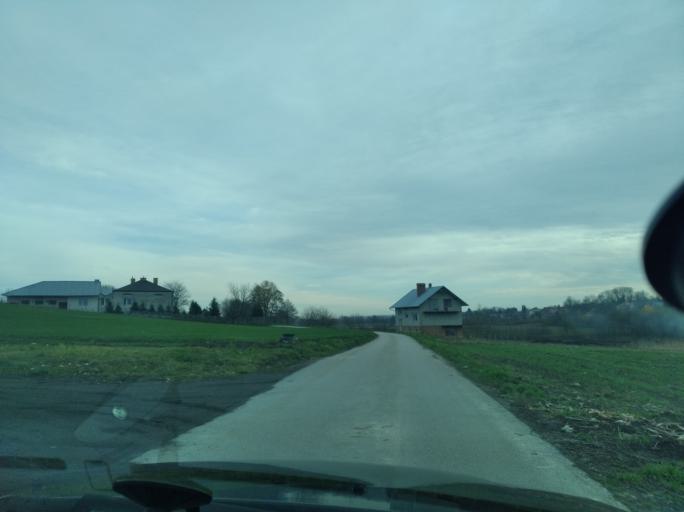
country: PL
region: Subcarpathian Voivodeship
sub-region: Powiat przeworski
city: Debow
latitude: 50.0492
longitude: 22.4249
